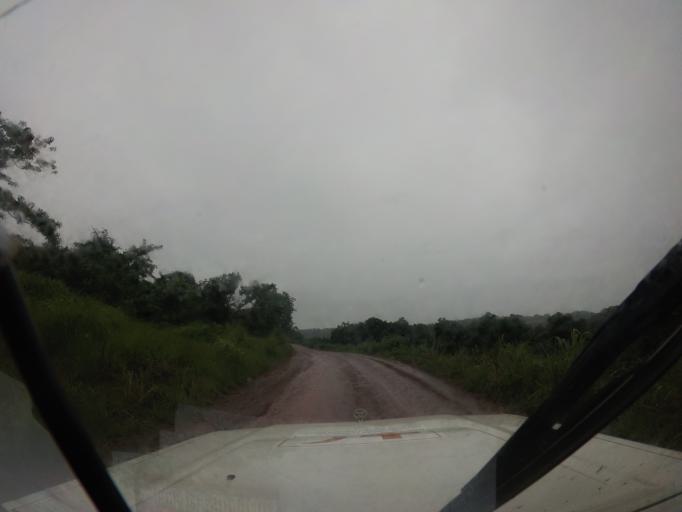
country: SL
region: Northern Province
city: Kabala
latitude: 9.6154
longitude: -11.5503
